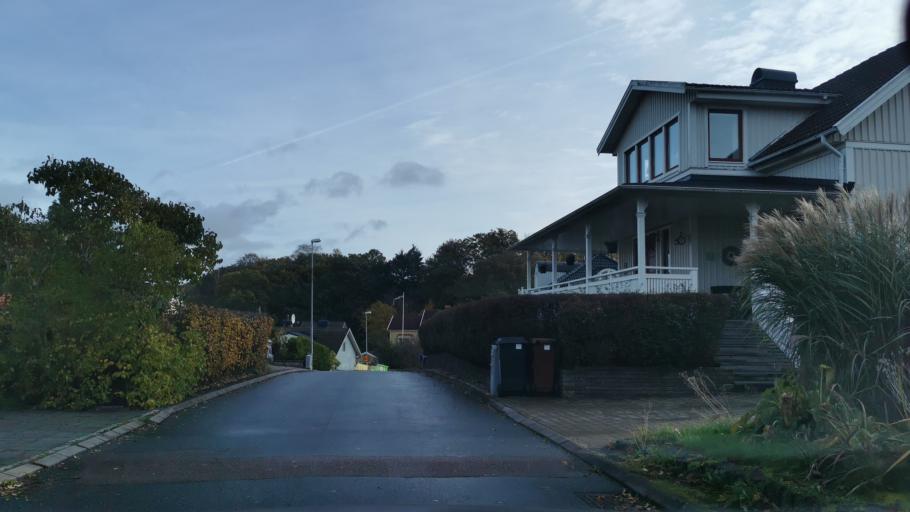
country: SE
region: Vaestra Goetaland
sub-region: Partille Kommun
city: Partille
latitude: 57.7309
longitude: 12.0801
